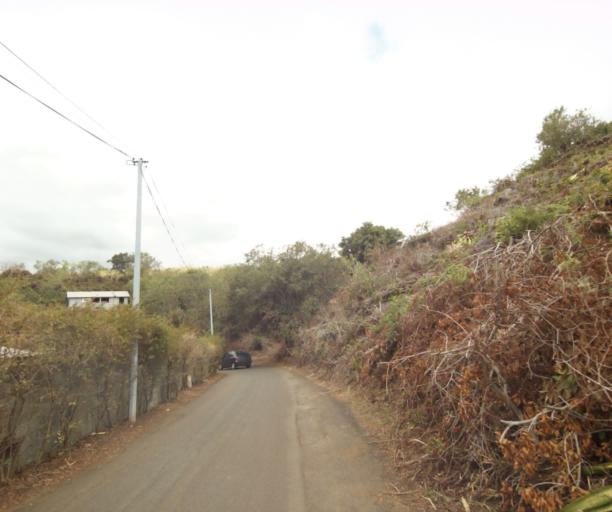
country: RE
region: Reunion
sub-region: Reunion
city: Saint-Paul
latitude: -21.0297
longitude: 55.3006
